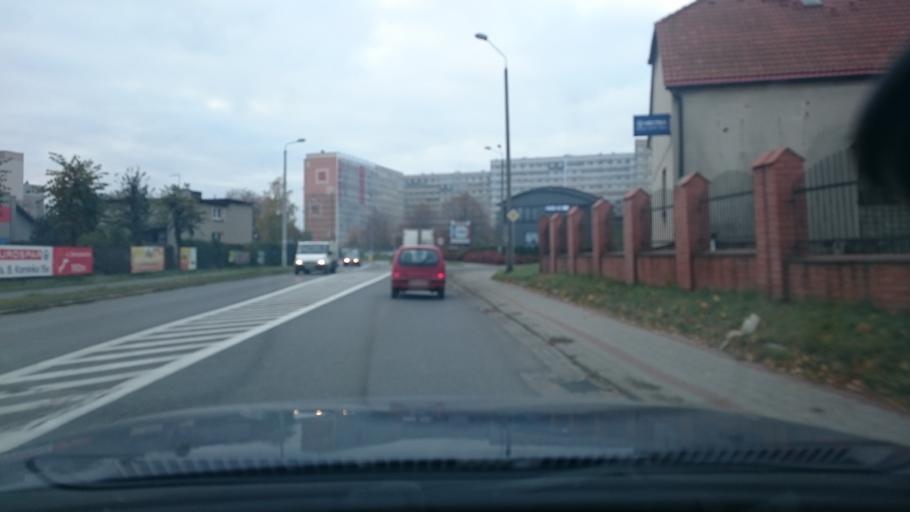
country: PL
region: Silesian Voivodeship
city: Zebrzydowice
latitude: 50.0957
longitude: 18.5151
